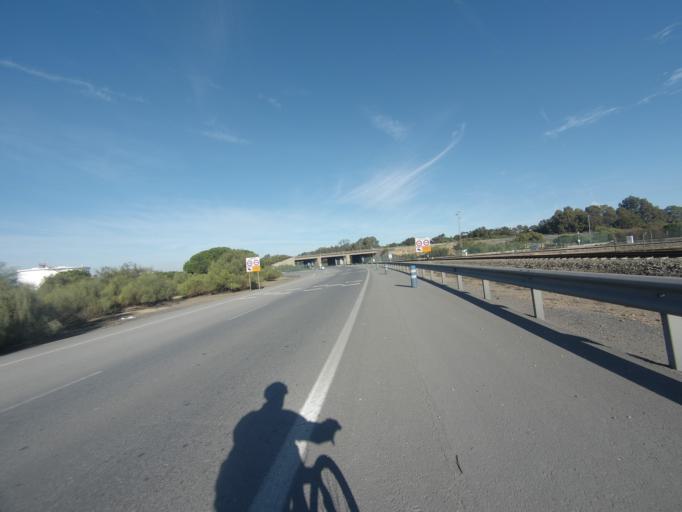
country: ES
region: Andalusia
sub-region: Provincia de Huelva
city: Punta Umbria
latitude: 37.2008
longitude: -6.9340
